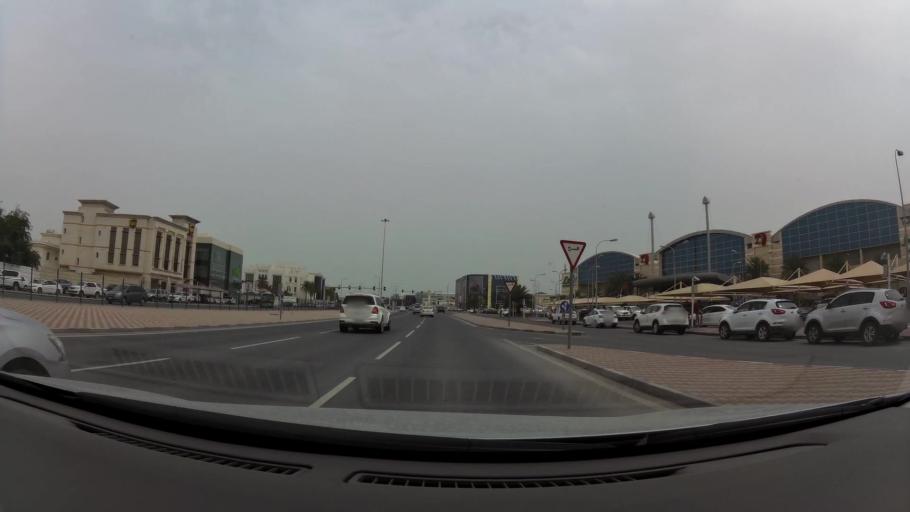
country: QA
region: Baladiyat ad Dawhah
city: Doha
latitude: 25.2548
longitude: 51.5448
